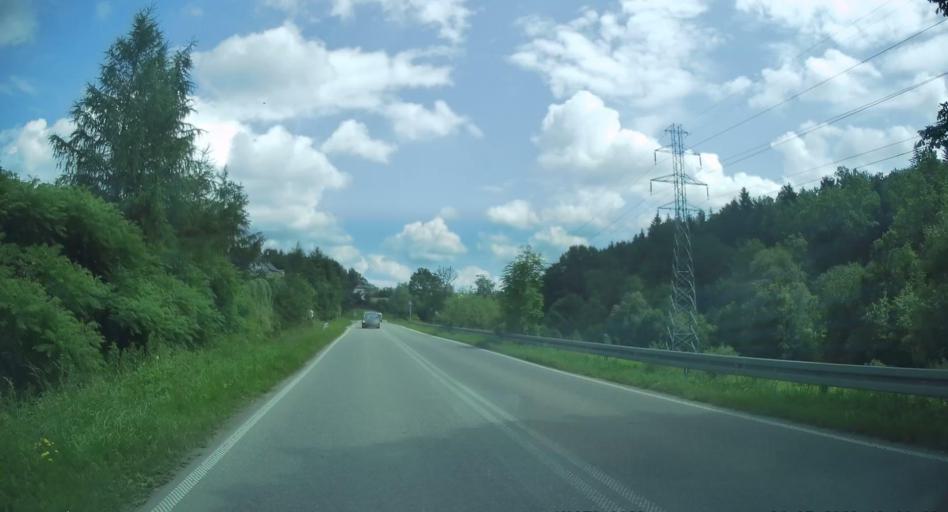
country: PL
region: Lesser Poland Voivodeship
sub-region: Powiat nowosadecki
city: Korzenna
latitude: 49.6671
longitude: 20.7732
